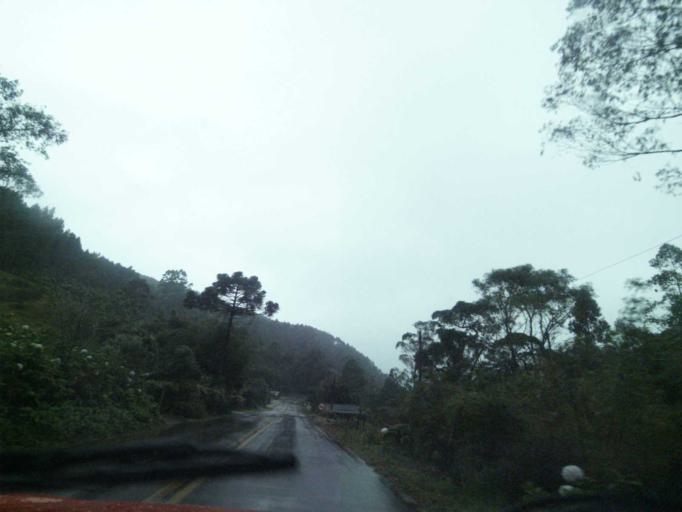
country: BR
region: Santa Catarina
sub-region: Anitapolis
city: Anitapolis
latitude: -27.8119
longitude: -49.0470
